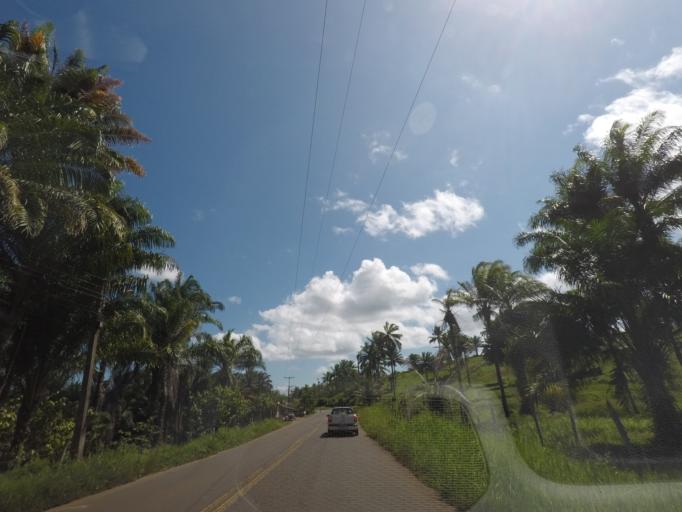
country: BR
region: Bahia
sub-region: Taperoa
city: Taperoa
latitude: -13.5593
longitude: -39.1047
